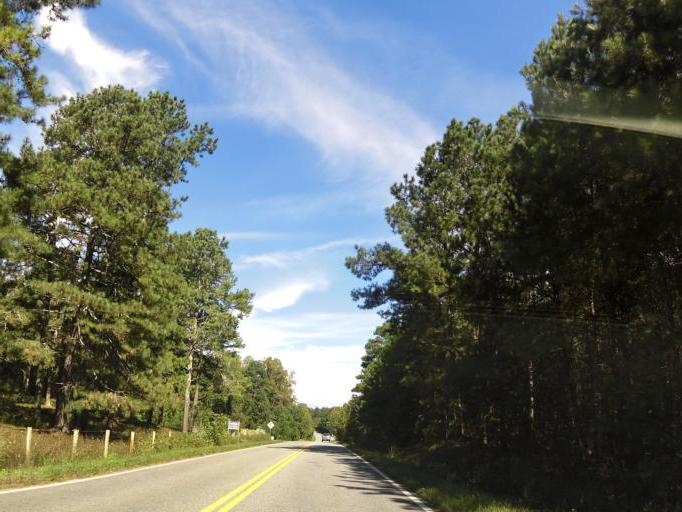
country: US
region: Georgia
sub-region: Pickens County
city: Nelson
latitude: 34.4184
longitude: -84.2786
